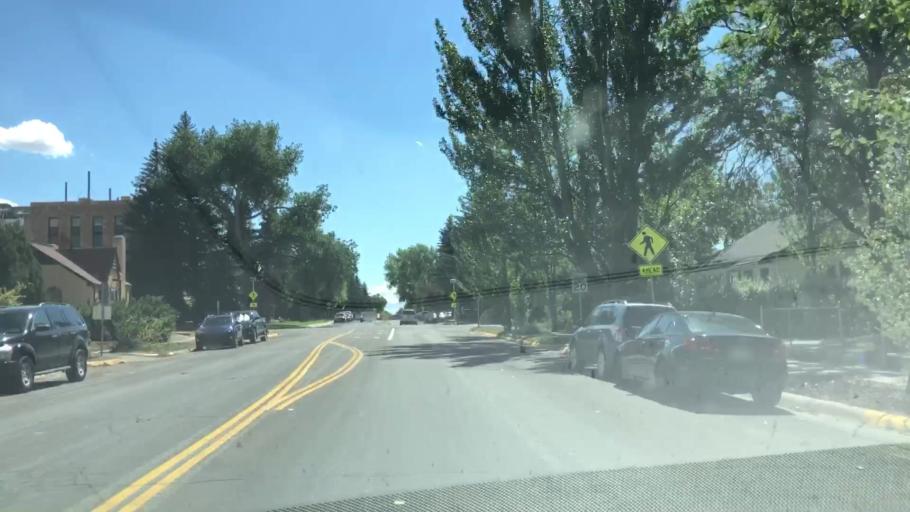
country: US
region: Wyoming
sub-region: Albany County
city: Laramie
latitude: 41.3160
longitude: -105.5852
